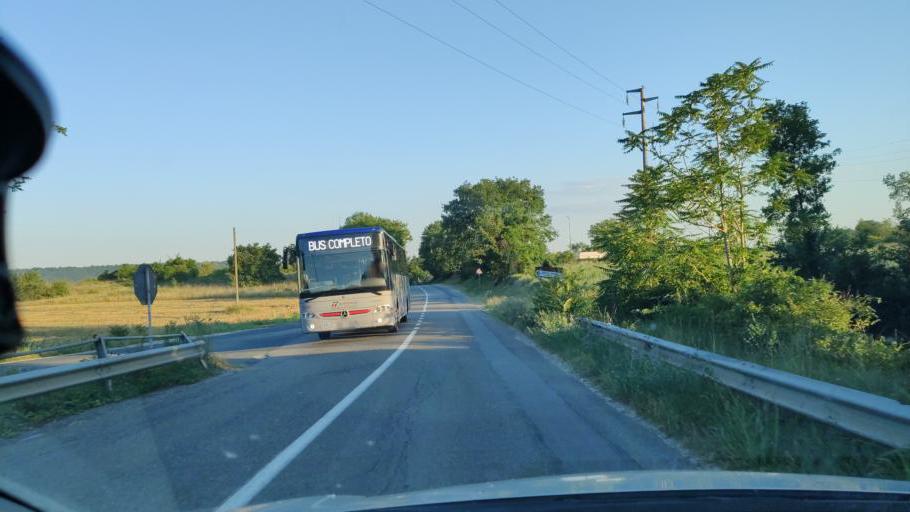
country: IT
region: Umbria
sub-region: Provincia di Terni
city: Attigliano
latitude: 42.5065
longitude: 12.3078
